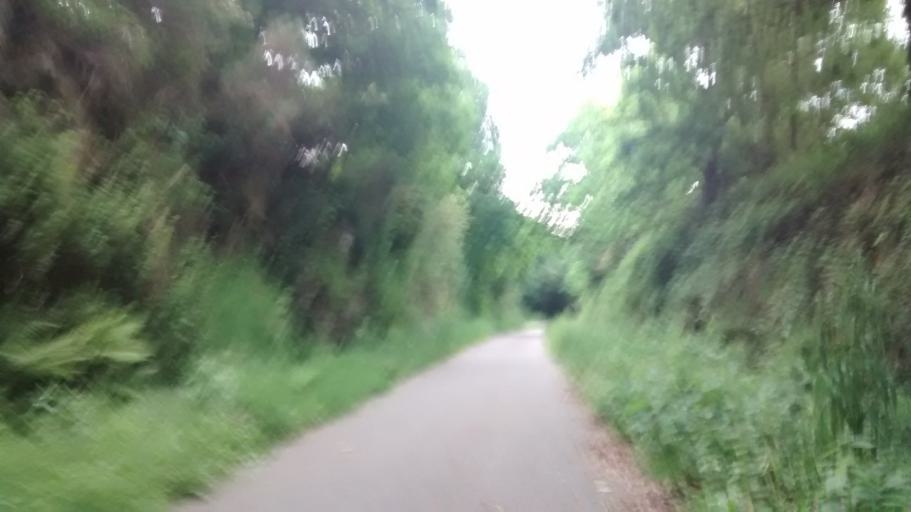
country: FR
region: Brittany
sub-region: Departement du Morbihan
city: Molac
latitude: 47.7305
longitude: -2.4194
